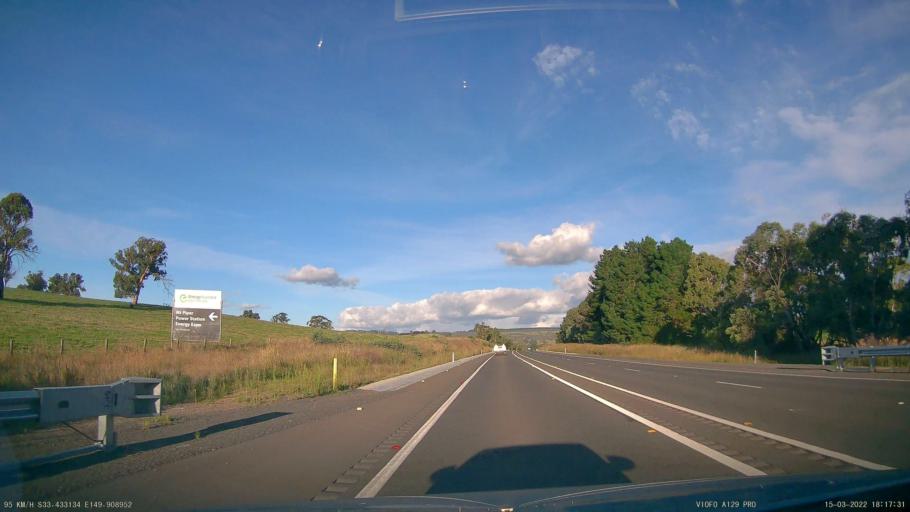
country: AU
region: New South Wales
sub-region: Lithgow
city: Portland
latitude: -33.4331
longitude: 149.9095
